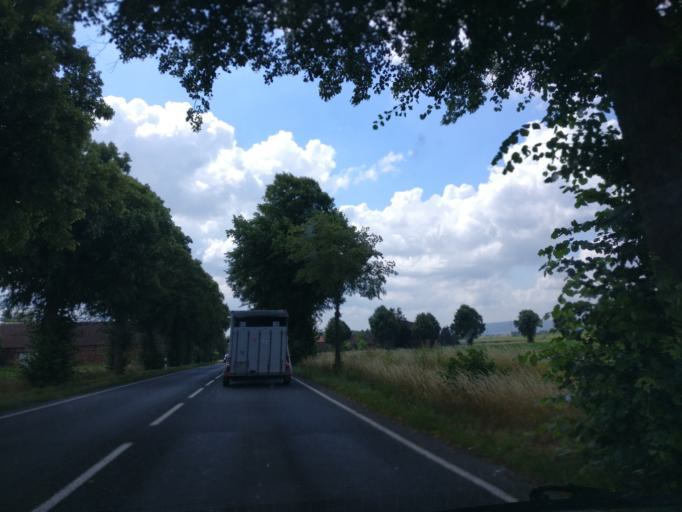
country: DE
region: Lower Saxony
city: Elze
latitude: 52.1550
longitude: 9.7391
